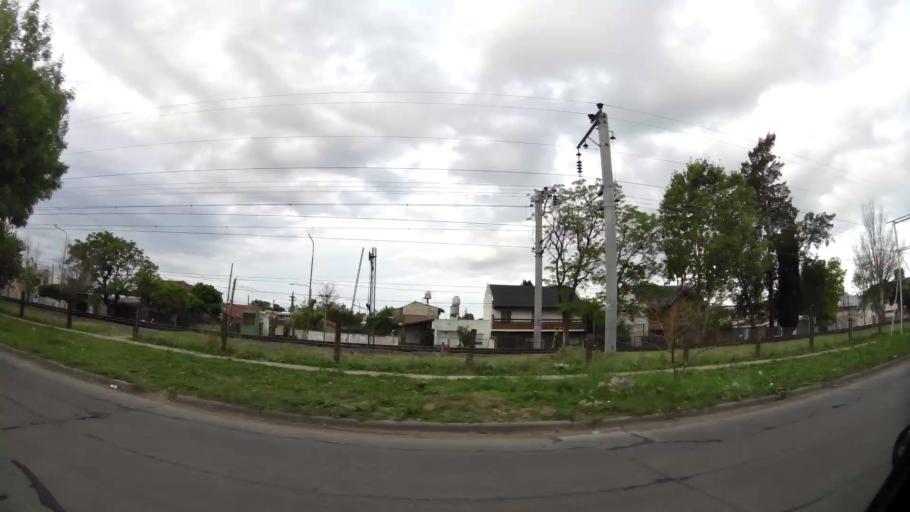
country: AR
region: Buenos Aires
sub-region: Partido de Quilmes
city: Quilmes
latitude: -34.7472
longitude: -58.2406
